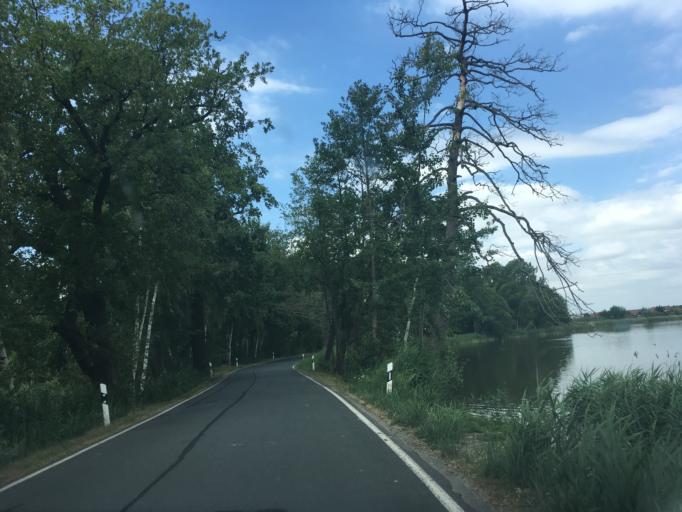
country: DE
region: Saxony
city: Tauscha
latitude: 51.2381
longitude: 13.7896
